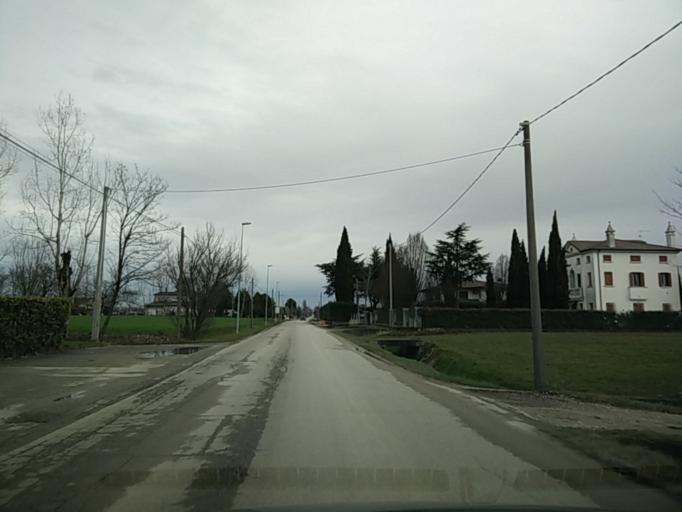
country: IT
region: Veneto
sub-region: Provincia di Treviso
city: Villa d'Asolo
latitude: 45.7558
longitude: 11.8894
